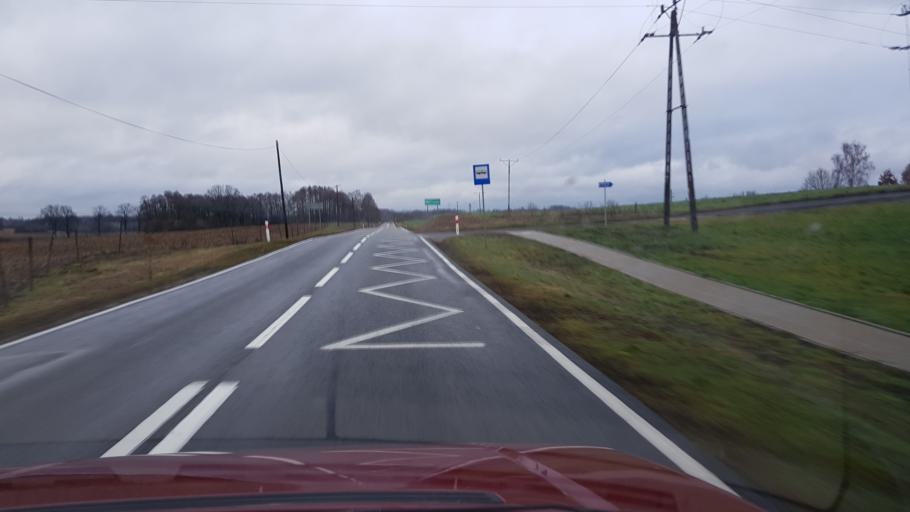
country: PL
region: West Pomeranian Voivodeship
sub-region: Powiat lobeski
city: Wegorzyno
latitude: 53.5130
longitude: 15.6425
